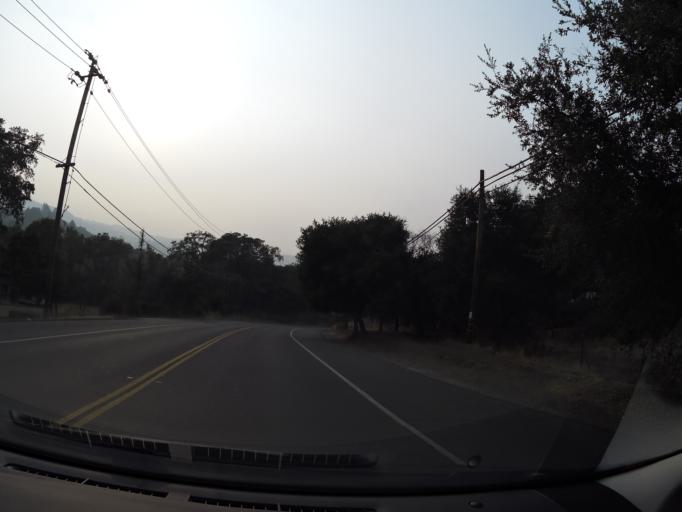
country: US
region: California
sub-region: Sonoma County
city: Eldridge
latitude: 38.3523
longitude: -122.5210
